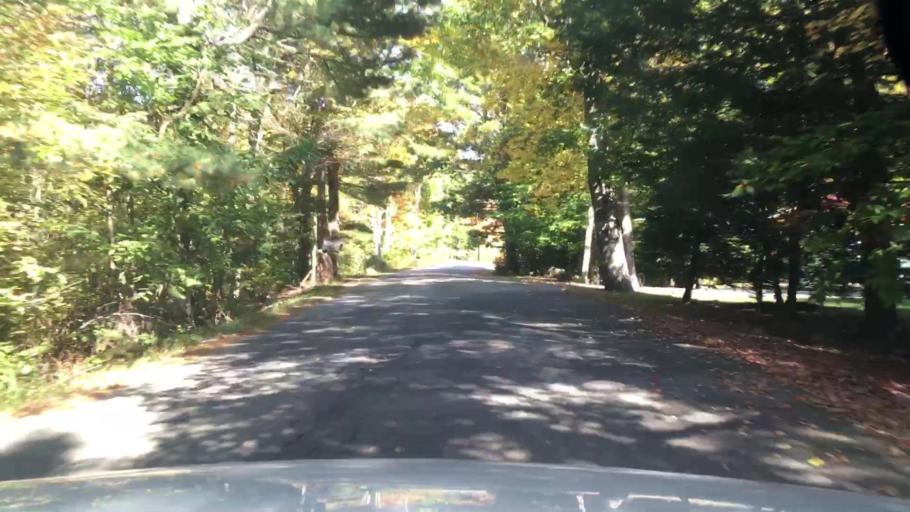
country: US
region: Maine
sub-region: Androscoggin County
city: Lisbon Falls
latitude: 44.0353
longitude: -69.9841
